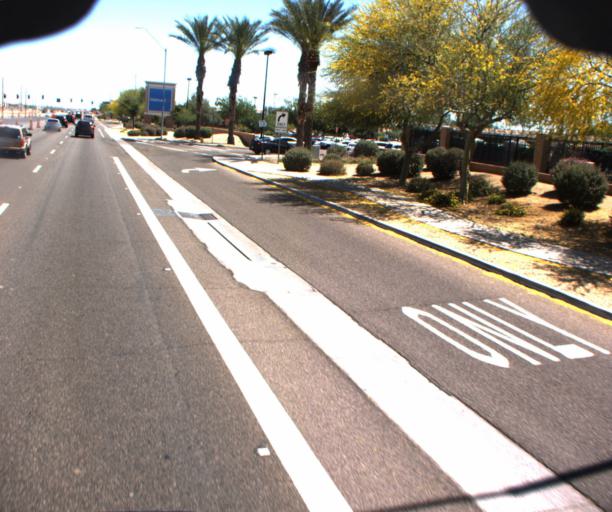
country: US
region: Arizona
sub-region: Maricopa County
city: Sun City West
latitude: 33.6436
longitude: -112.3568
